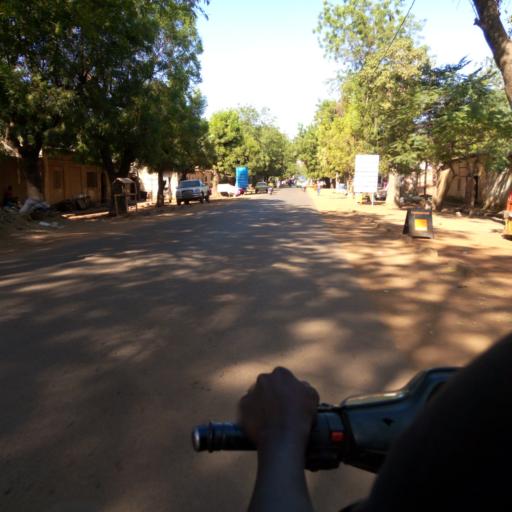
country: ML
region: Bamako
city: Bamako
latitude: 12.6554
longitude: -8.0166
